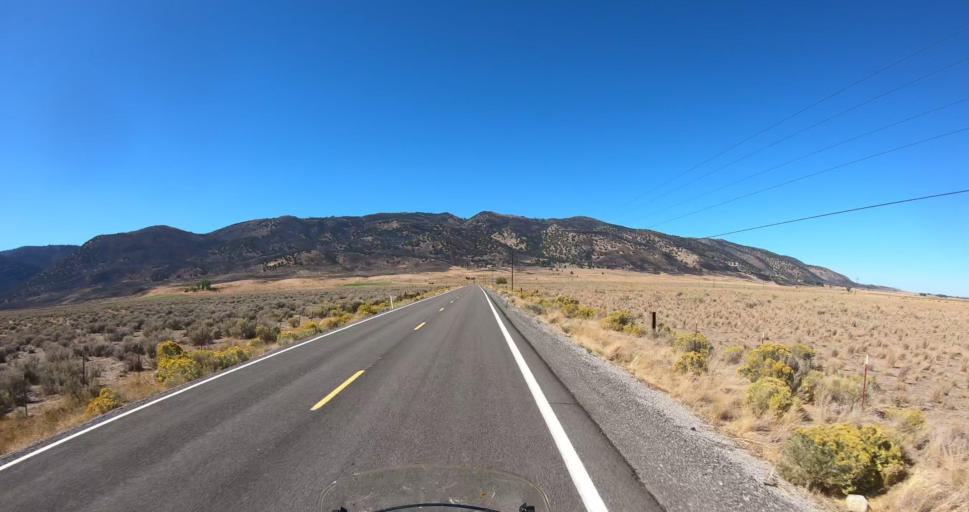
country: US
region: Oregon
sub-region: Lake County
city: Lakeview
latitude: 42.6178
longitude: -120.4950
